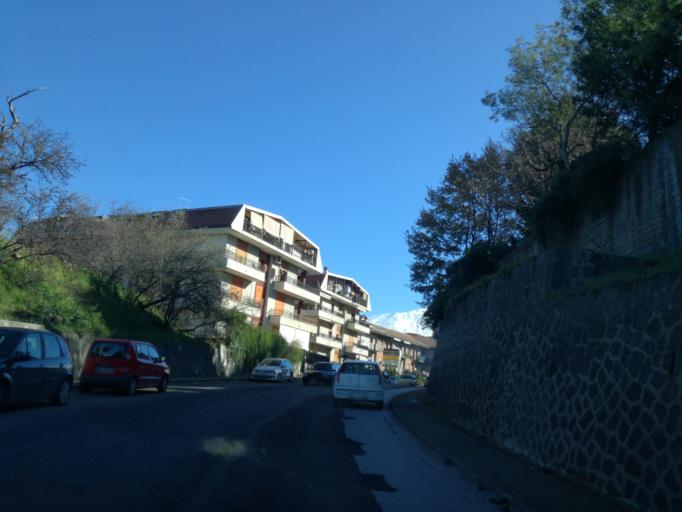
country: IT
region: Sicily
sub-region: Catania
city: Bronte
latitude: 37.7821
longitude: 14.8328
